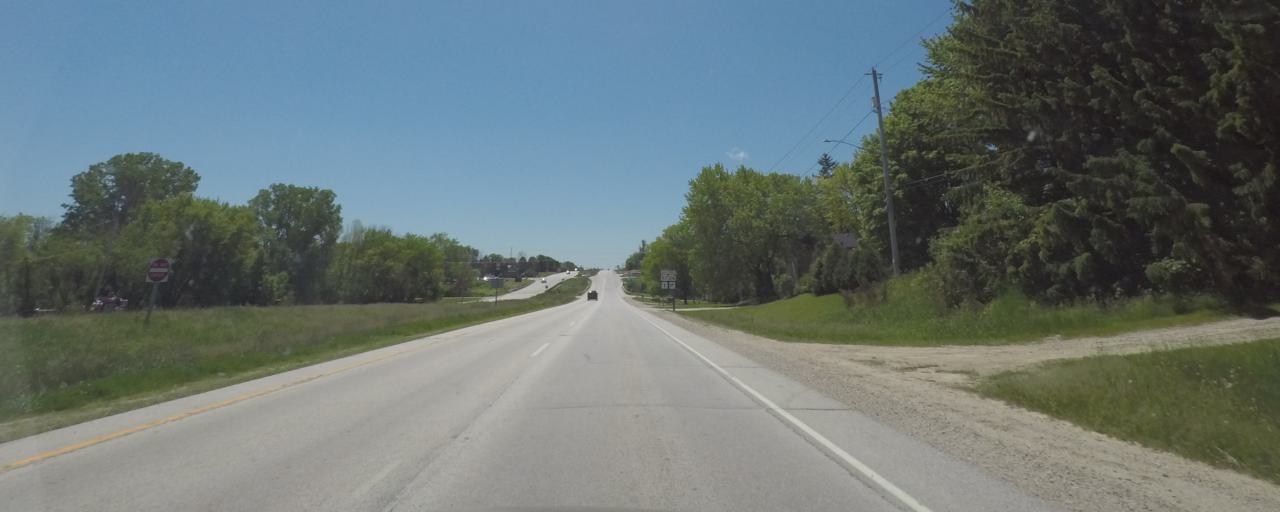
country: US
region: Wisconsin
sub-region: Sheboygan County
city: Plymouth
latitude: 43.6779
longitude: -87.9409
